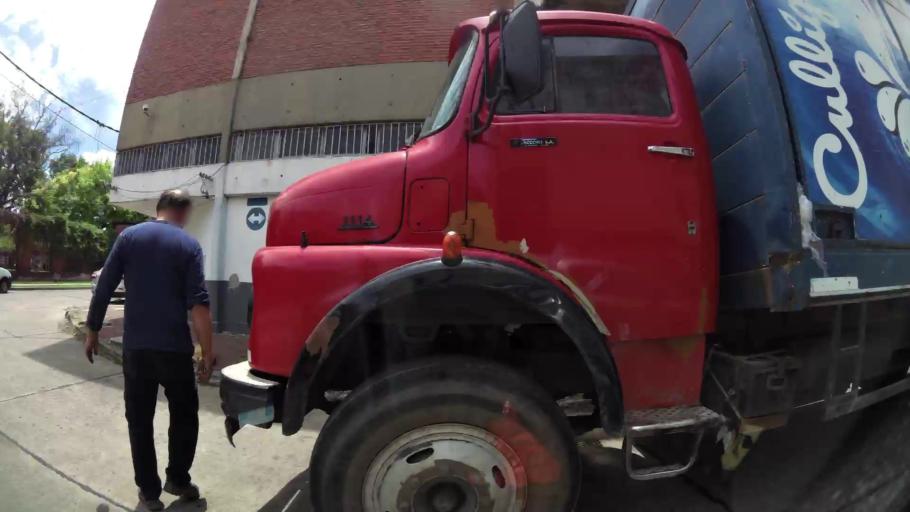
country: AR
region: Santa Fe
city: Gobernador Galvez
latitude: -32.9986
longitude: -60.6210
